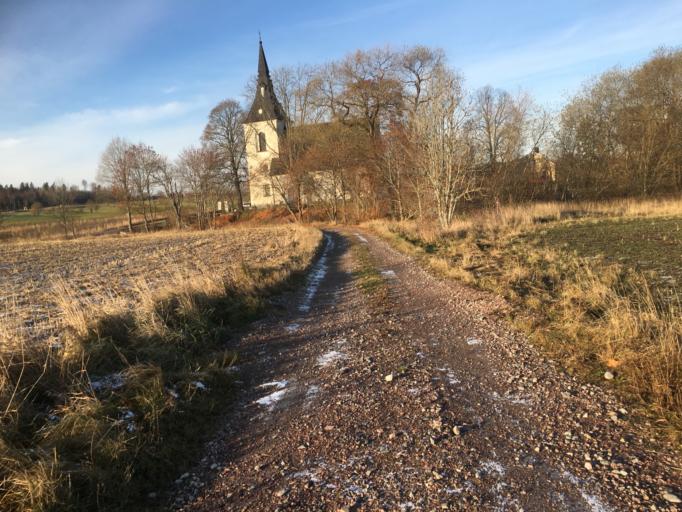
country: SE
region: Vaestmanland
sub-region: Vasteras
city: Vasteras
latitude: 59.6434
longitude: 16.4812
